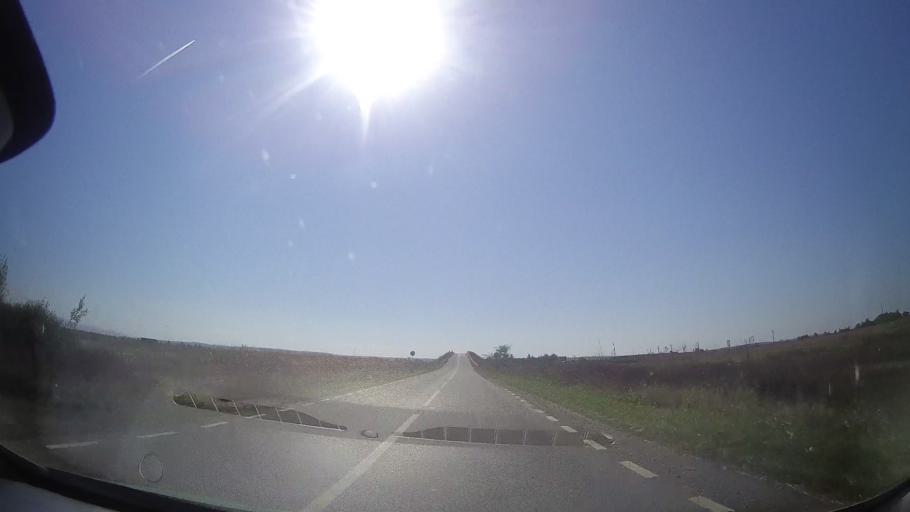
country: RO
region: Timis
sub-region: Comuna Bethausen
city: Bethausen
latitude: 45.8187
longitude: 21.9597
